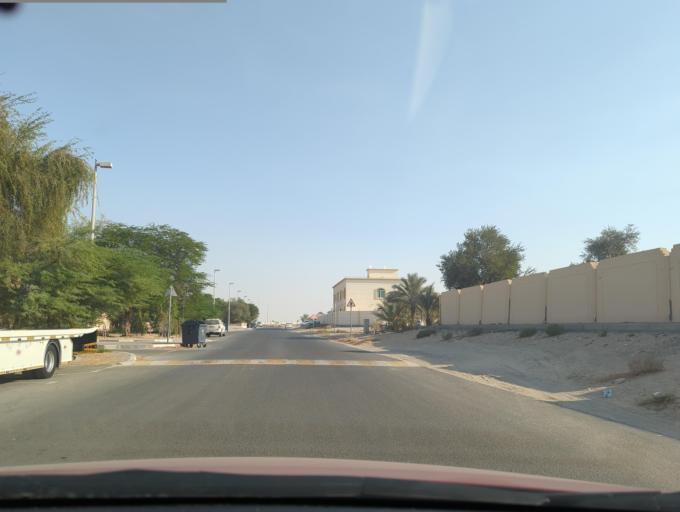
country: AE
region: Abu Dhabi
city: Abu Dhabi
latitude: 24.3973
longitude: 54.7427
